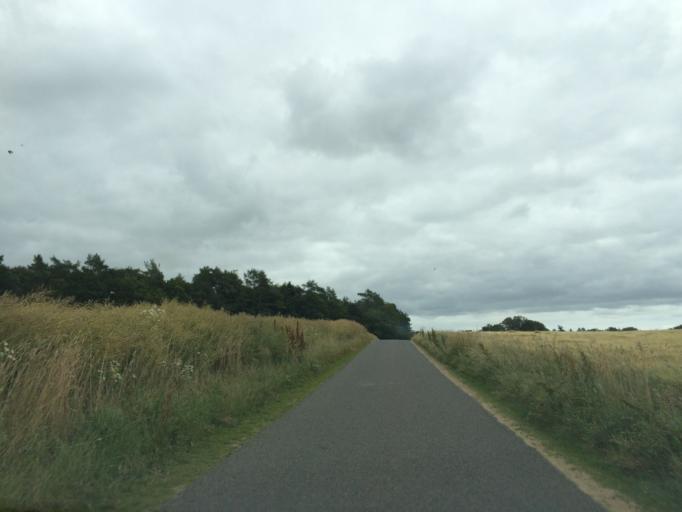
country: DK
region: Central Jutland
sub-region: Silkeborg Kommune
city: Svejbaek
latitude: 56.2061
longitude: 9.6389
